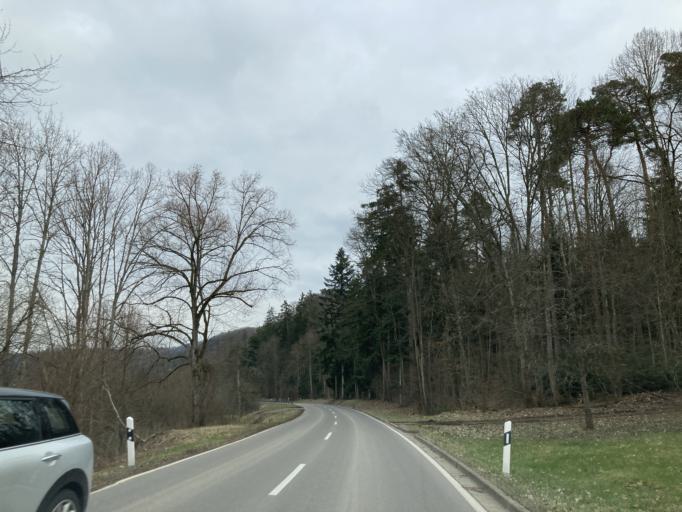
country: DE
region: Baden-Wuerttemberg
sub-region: Tuebingen Region
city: Hirrlingen
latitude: 48.4552
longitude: 8.8793
